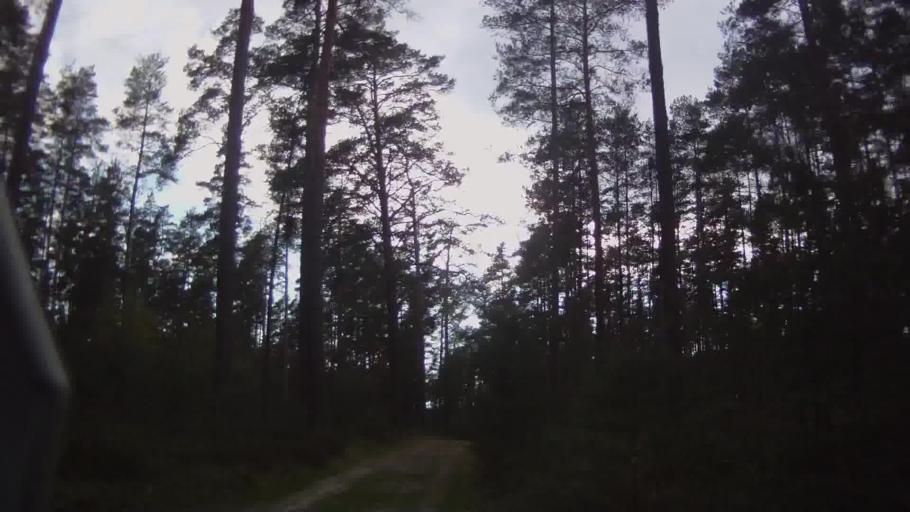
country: LV
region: Riga
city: Jaunciems
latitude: 57.0681
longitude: 24.1780
